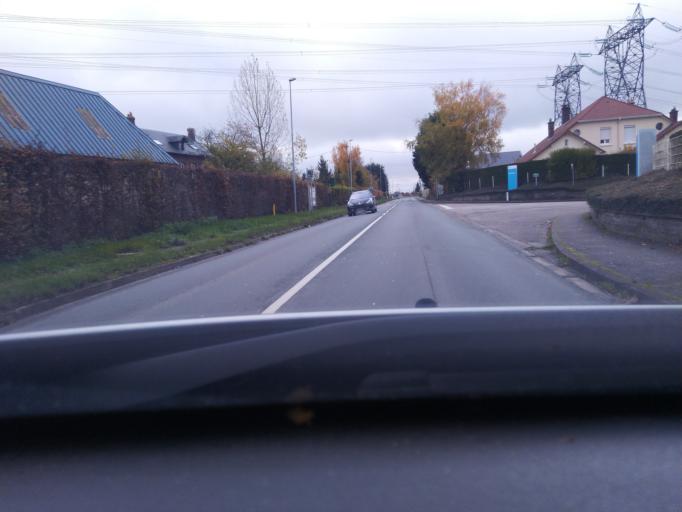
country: FR
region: Haute-Normandie
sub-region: Departement de la Seine-Maritime
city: Maromme
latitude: 49.4855
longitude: 1.0114
